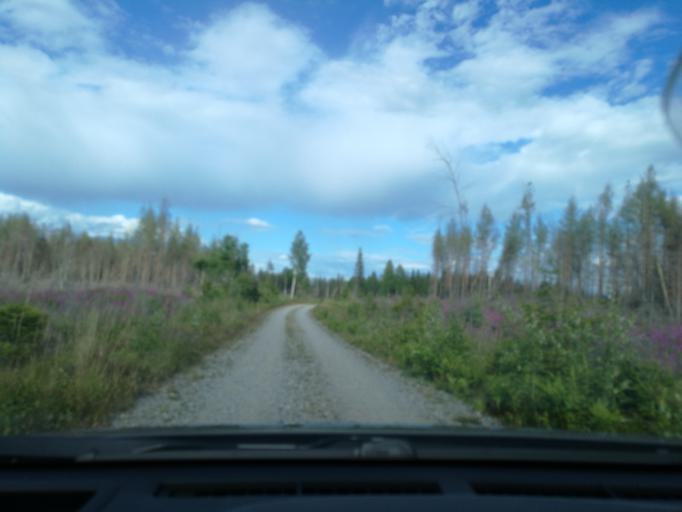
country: SE
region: Vaestmanland
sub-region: Surahammars Kommun
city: Ramnas
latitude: 59.8490
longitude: 16.2747
